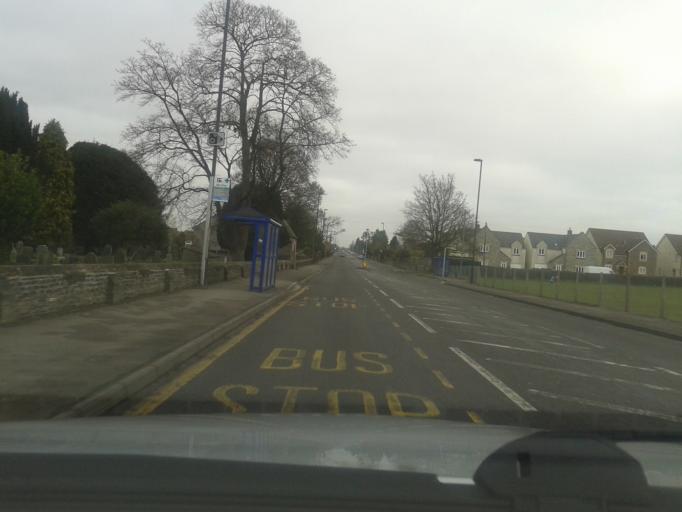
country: GB
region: England
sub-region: South Gloucestershire
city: Winterbourne
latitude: 51.5241
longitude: -2.4717
